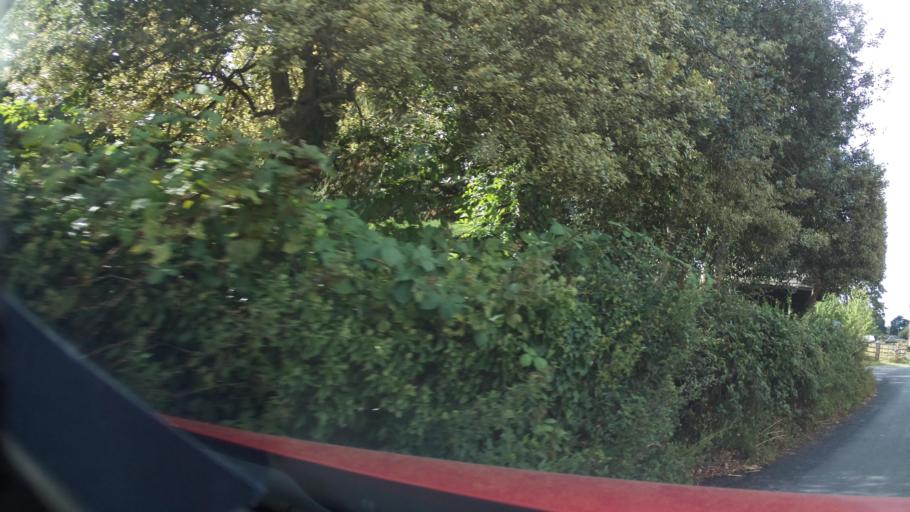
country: GB
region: England
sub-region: Leicestershire
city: Loughborough
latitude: 52.7931
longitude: -1.1948
